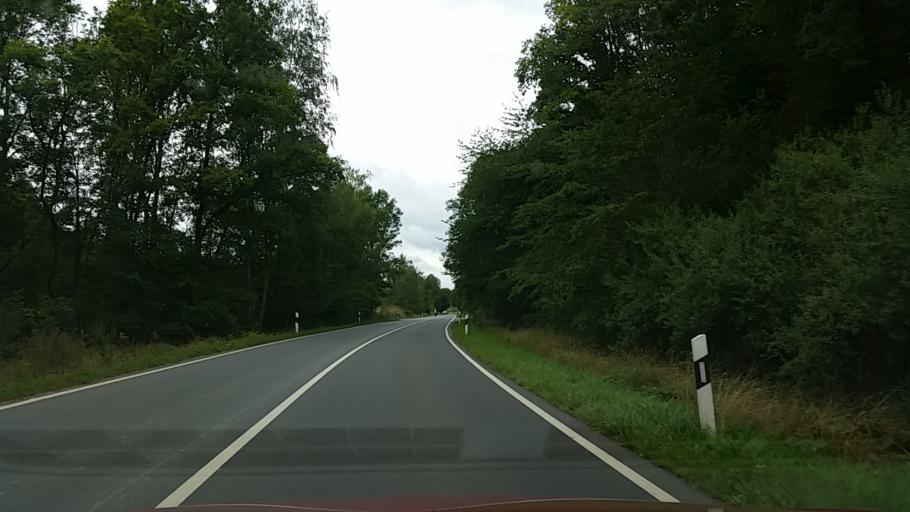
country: DE
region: Lower Saxony
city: Vienenburg
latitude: 51.9472
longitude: 10.5193
